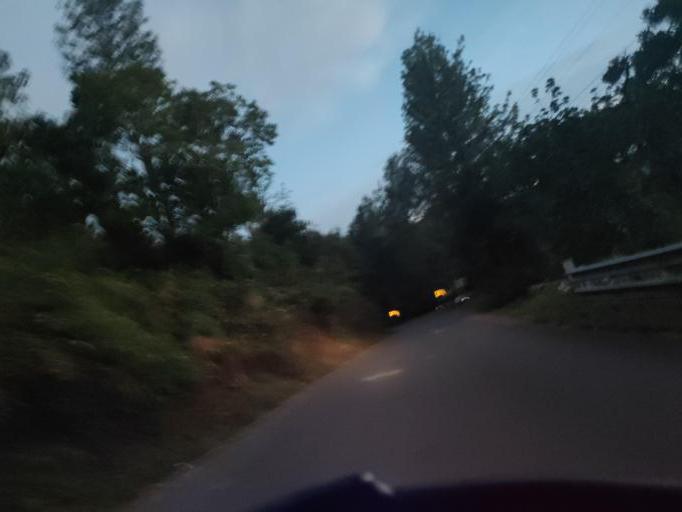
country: IN
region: Tamil Nadu
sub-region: Dindigul
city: Kodaikanal
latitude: 10.2906
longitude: 77.5358
